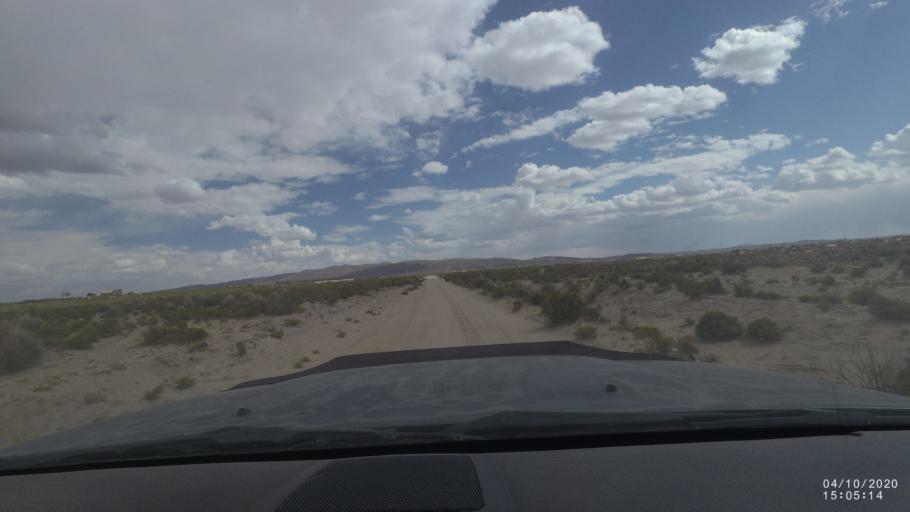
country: BO
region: Oruro
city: Poopo
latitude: -18.6918
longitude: -67.5544
